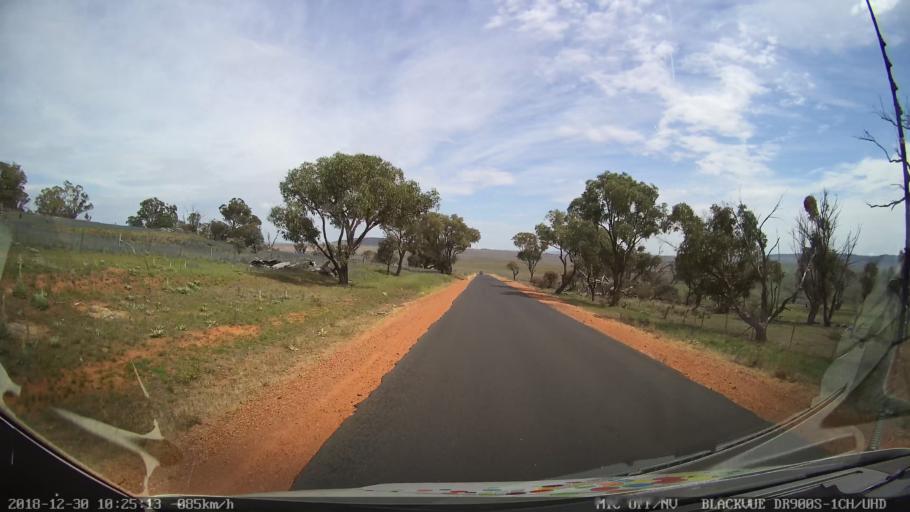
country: AU
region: New South Wales
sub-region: Snowy River
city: Berridale
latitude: -36.5269
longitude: 148.9606
